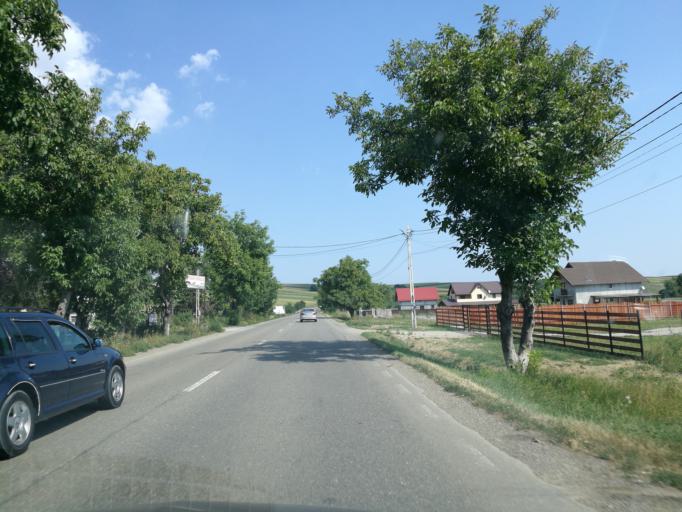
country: RO
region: Neamt
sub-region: Comuna Baltatesti
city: Valea Seaca
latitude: 47.1420
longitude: 26.3185
